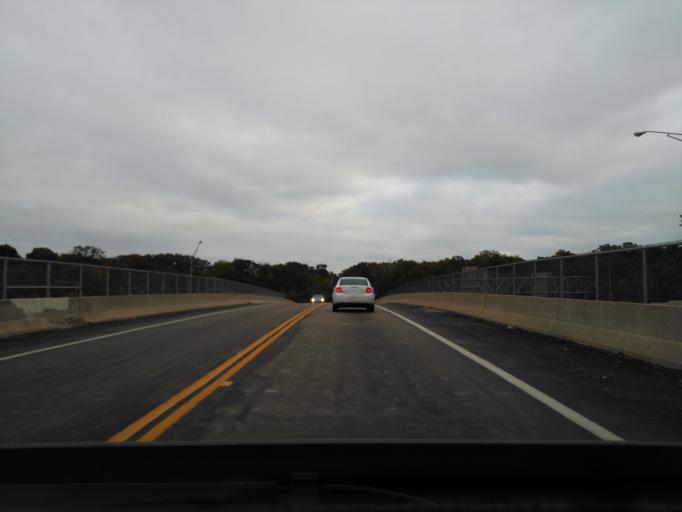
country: US
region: Missouri
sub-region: Saint Louis County
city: Sunset Hills
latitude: 38.5549
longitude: -90.4163
